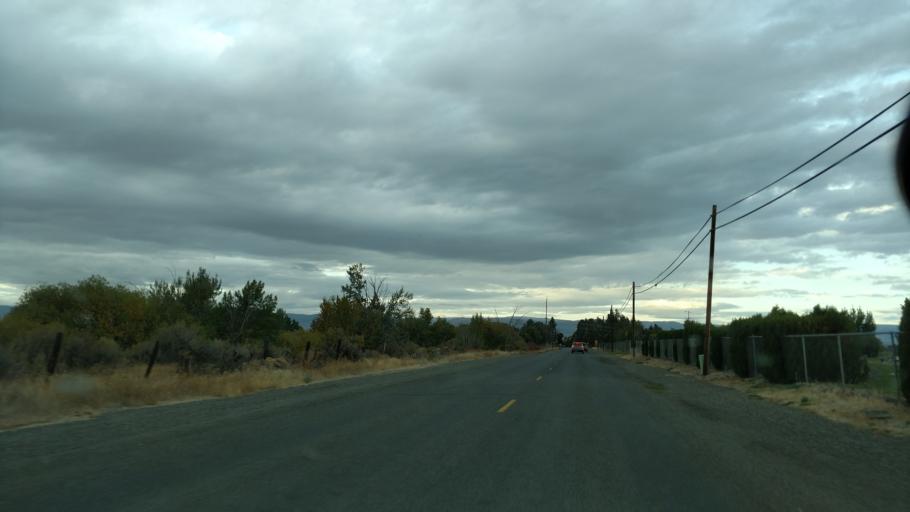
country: US
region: Washington
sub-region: Kittitas County
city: Ellensburg
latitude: 47.0117
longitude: -120.5213
